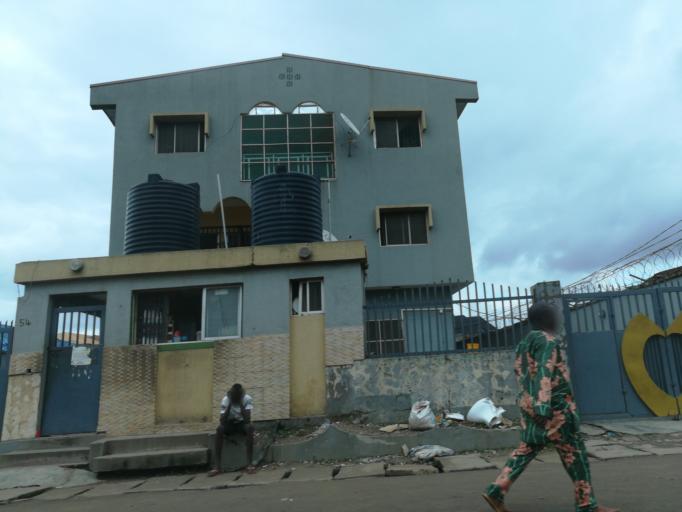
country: NG
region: Lagos
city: Agege
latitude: 6.6124
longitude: 3.3131
